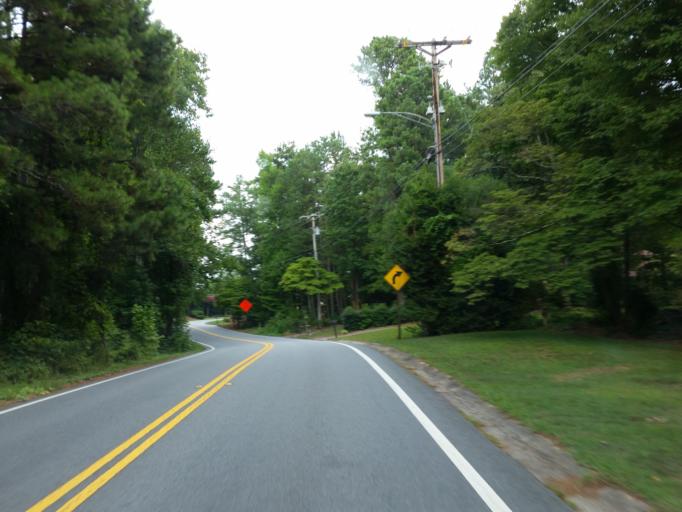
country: US
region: Georgia
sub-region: Fulton County
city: Roswell
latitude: 34.0403
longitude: -84.4397
